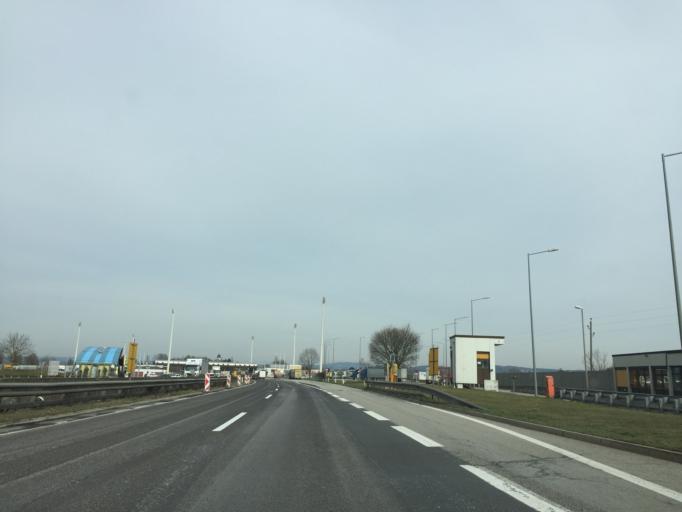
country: AT
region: Upper Austria
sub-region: Politischer Bezirk Scharding
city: Sankt Marienkirchen bei Schaerding
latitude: 48.4024
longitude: 13.4277
